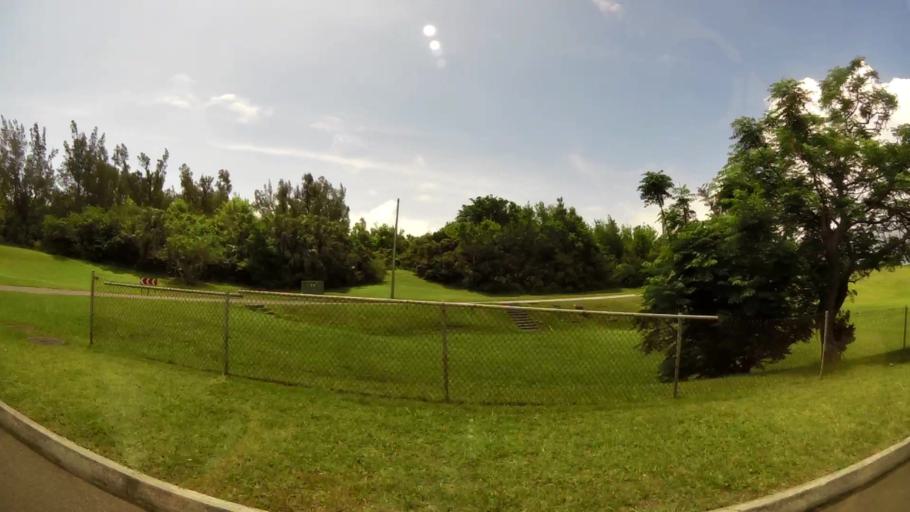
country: BM
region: Saint George
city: Saint George
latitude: 32.3637
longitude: -64.6585
